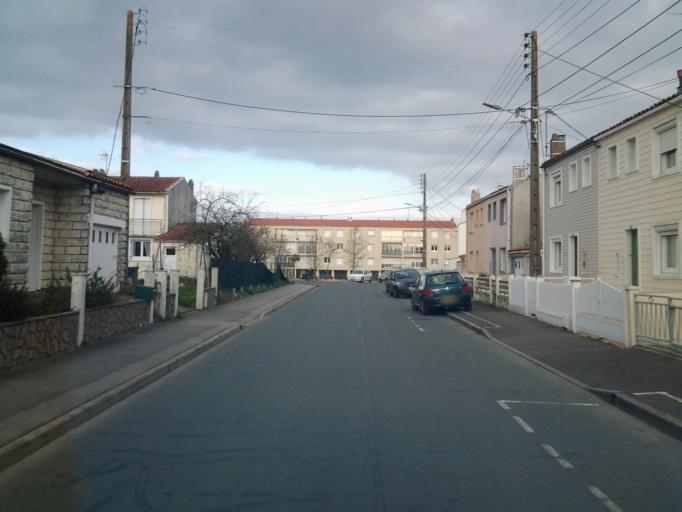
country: FR
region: Pays de la Loire
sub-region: Departement de la Vendee
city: La Roche-sur-Yon
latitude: 46.6793
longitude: -1.4450
